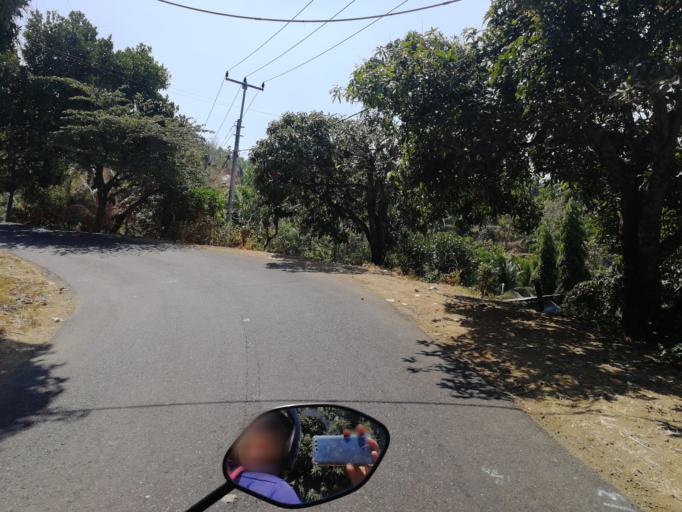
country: ID
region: Bali
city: Banjar Kedisan
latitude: -8.1400
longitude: 115.3199
